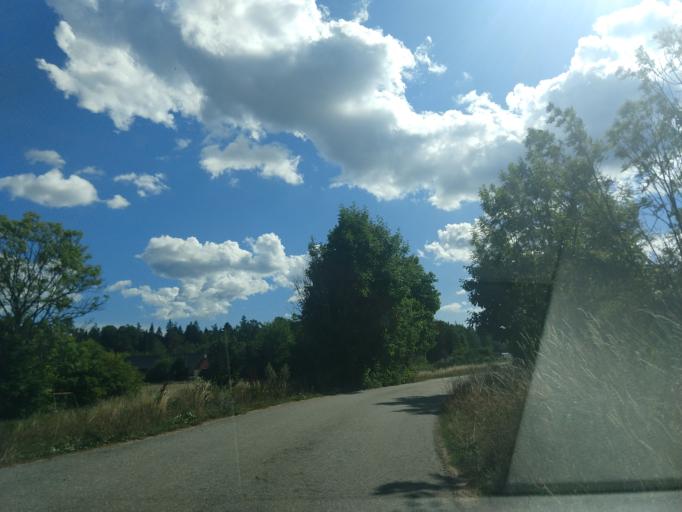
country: SE
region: Blekinge
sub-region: Ronneby Kommun
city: Brakne-Hoby
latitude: 56.2639
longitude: 15.1959
